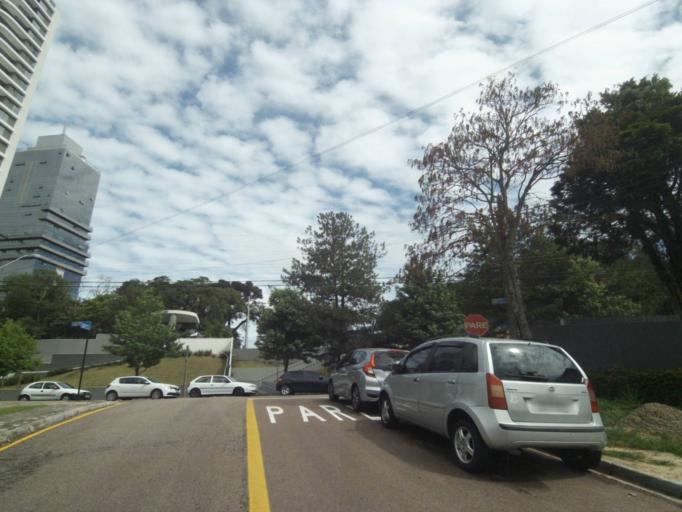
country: BR
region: Parana
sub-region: Curitiba
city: Curitiba
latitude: -25.4370
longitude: -49.3104
